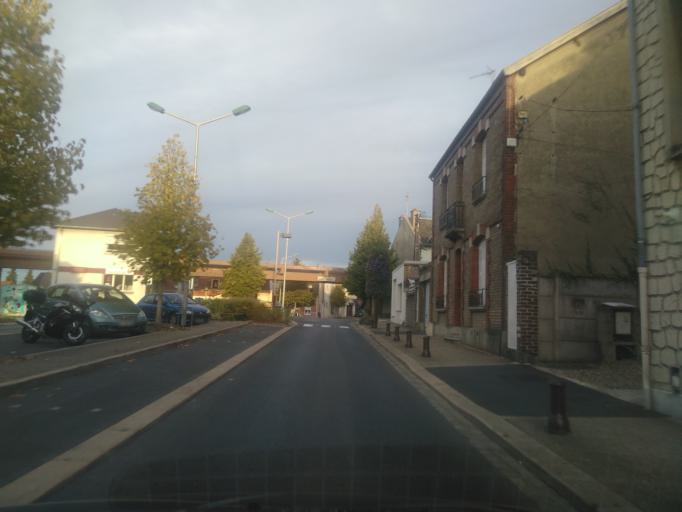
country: FR
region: Picardie
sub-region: Departement de l'Aisne
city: Laon
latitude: 49.5694
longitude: 3.6291
